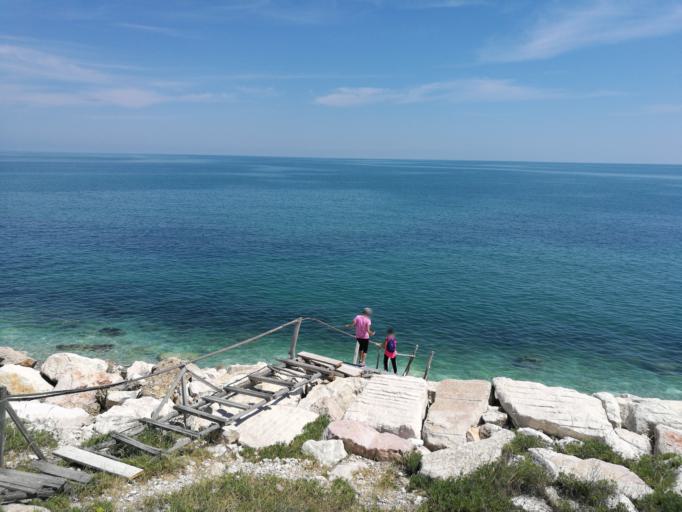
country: IT
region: Abruzzo
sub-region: Provincia di Chieti
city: Marina di San Vito
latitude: 42.3222
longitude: 14.4299
